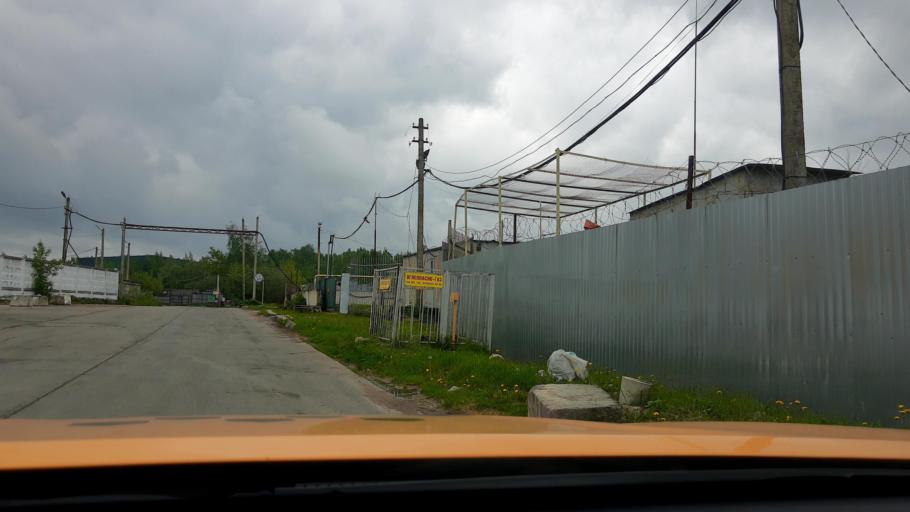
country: RU
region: Moskovskaya
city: L'vovskiy
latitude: 55.3271
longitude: 37.4978
